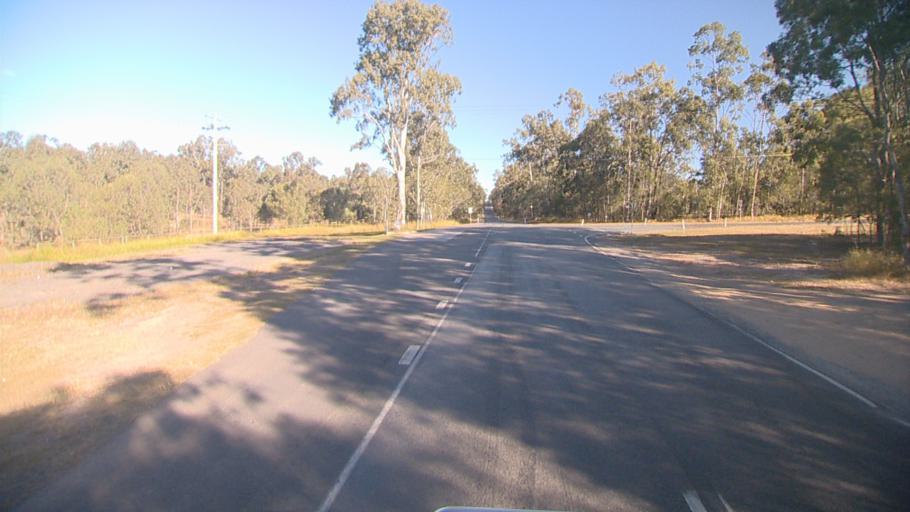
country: AU
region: Queensland
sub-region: Logan
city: North Maclean
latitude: -27.7921
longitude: 153.0271
